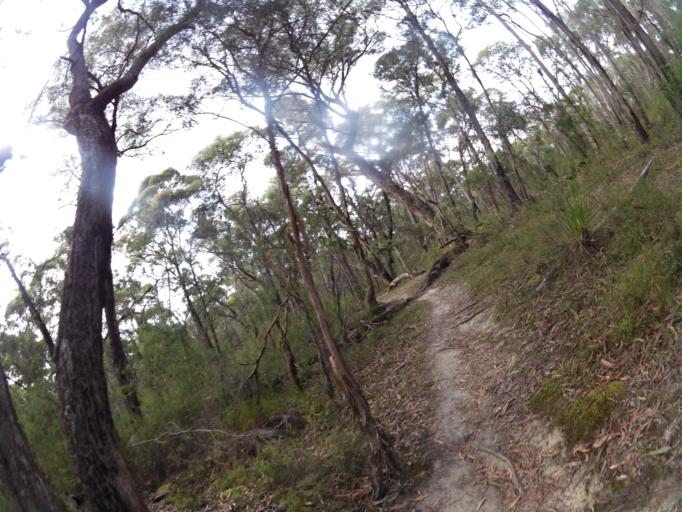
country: AU
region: Victoria
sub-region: Colac-Otway
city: Colac
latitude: -38.4894
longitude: 143.7017
